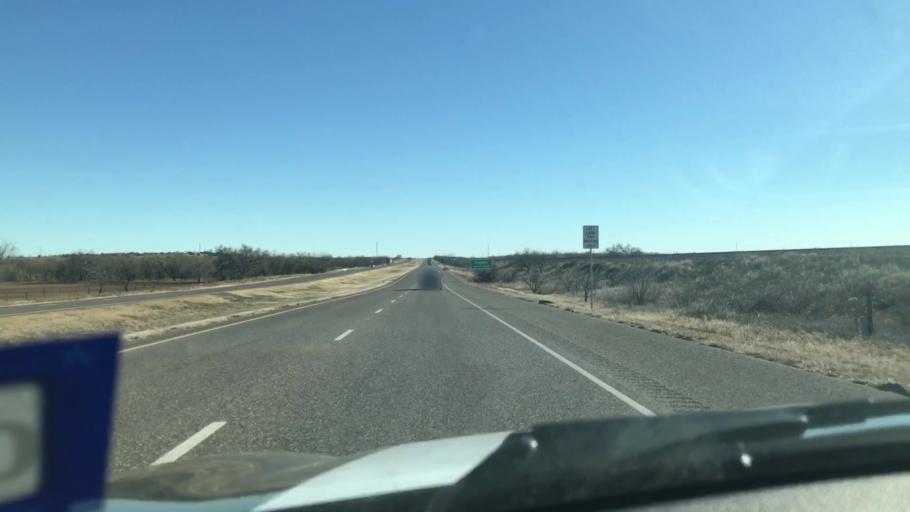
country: US
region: Texas
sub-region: Scurry County
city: Snyder
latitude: 32.8147
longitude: -100.9755
